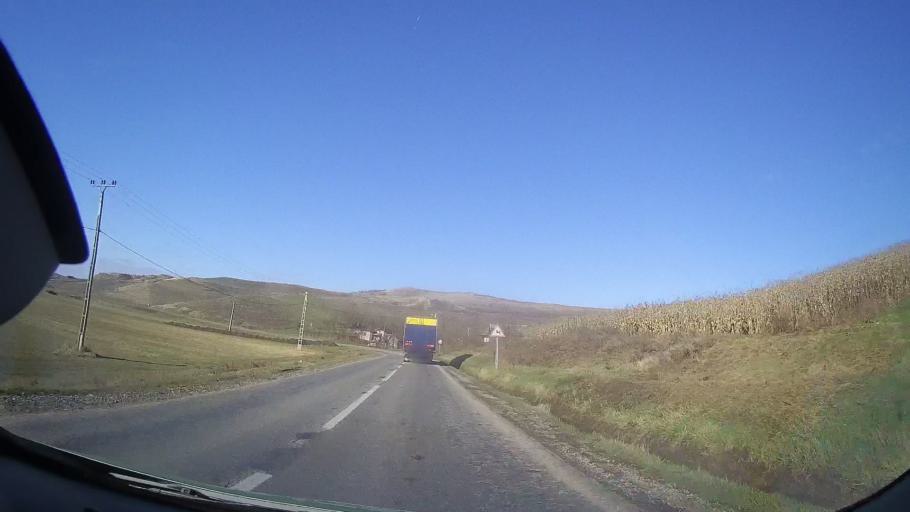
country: RO
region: Cluj
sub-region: Comuna Camarasu
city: Camarasu
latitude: 46.8000
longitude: 24.1640
